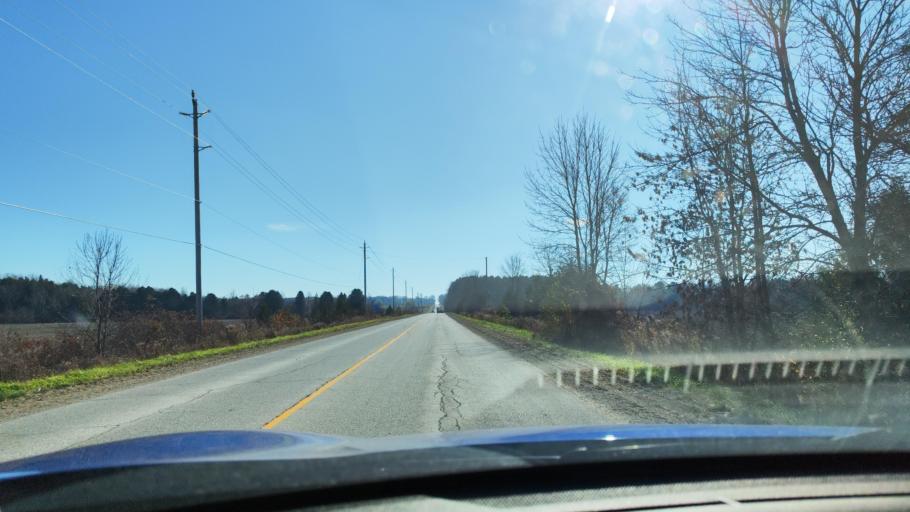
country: CA
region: Ontario
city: Wasaga Beach
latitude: 44.4691
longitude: -80.0057
